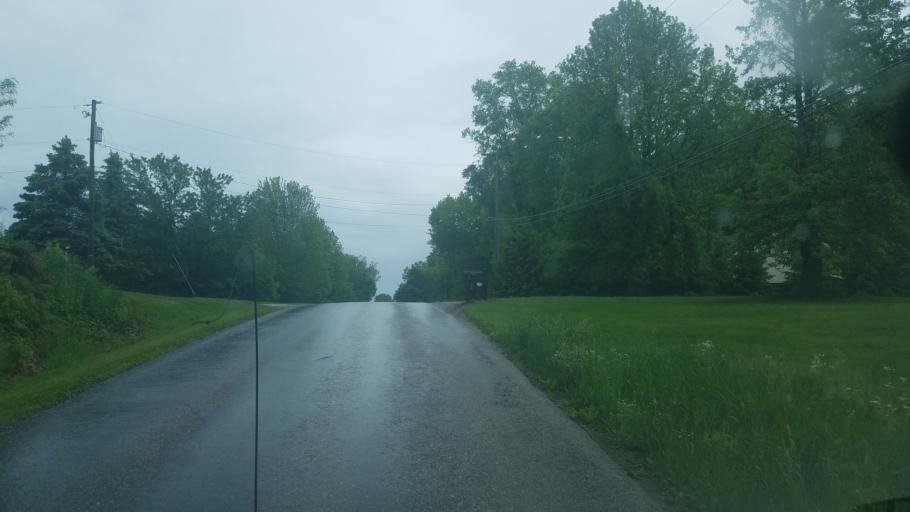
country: US
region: Ohio
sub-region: Wayne County
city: Smithville
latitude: 40.8129
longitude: -81.8772
